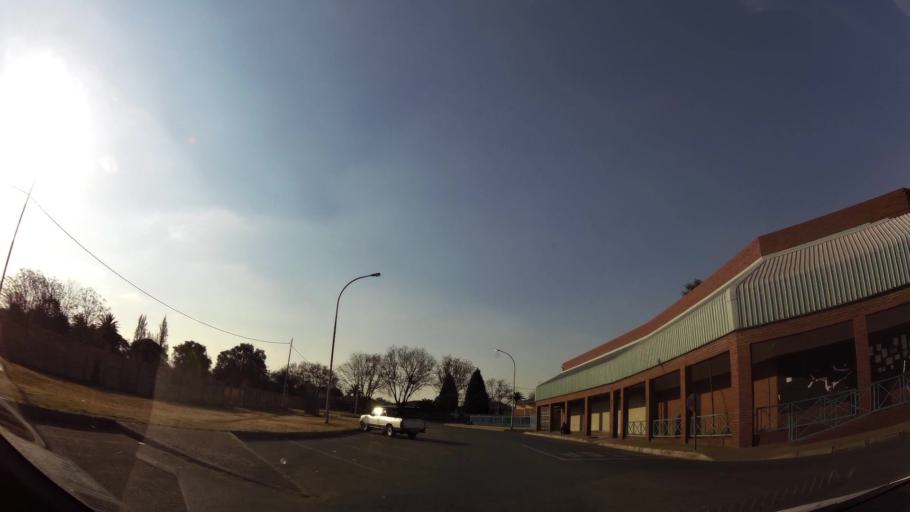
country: ZA
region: Gauteng
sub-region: Ekurhuleni Metropolitan Municipality
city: Brakpan
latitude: -26.2539
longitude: 28.3777
